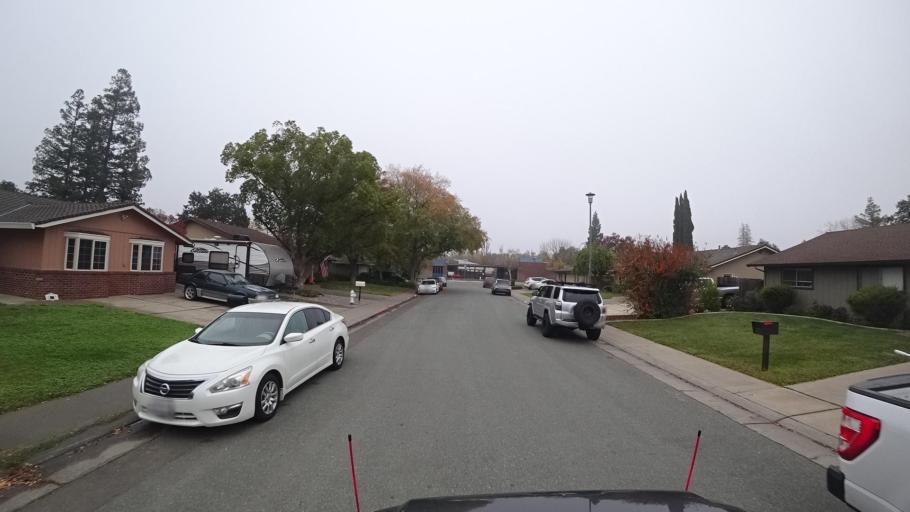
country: US
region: California
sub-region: Sacramento County
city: Elk Grove
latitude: 38.3996
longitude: -121.3700
